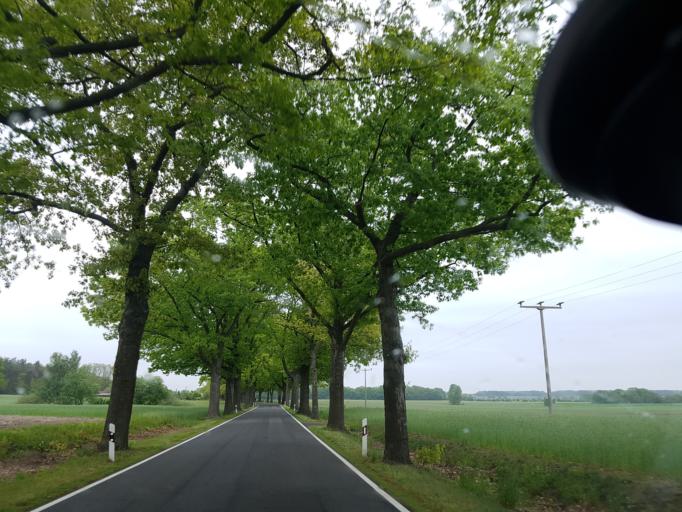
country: DE
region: Brandenburg
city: Spremberg
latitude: 51.6566
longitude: 14.3341
